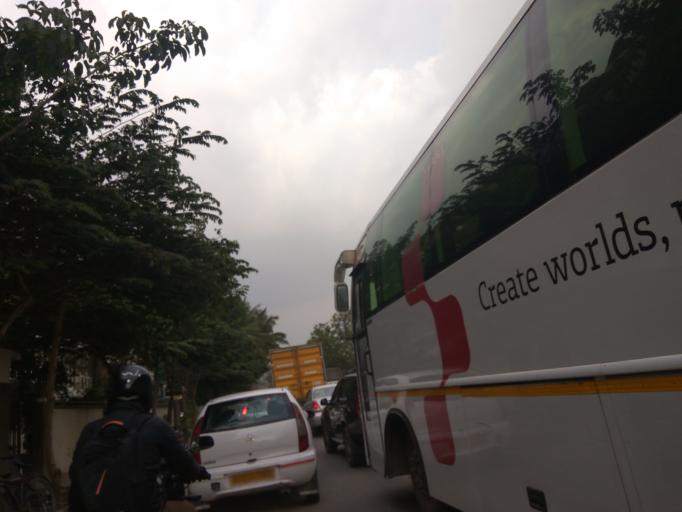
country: IN
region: Karnataka
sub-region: Bangalore Urban
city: Bangalore
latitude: 12.9744
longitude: 77.7042
